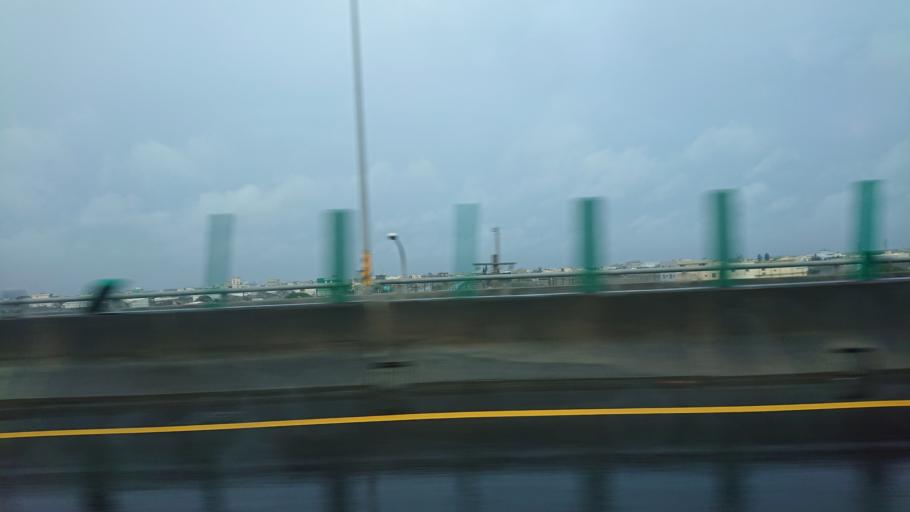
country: TW
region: Taiwan
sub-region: Changhua
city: Chang-hua
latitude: 24.1407
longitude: 120.4452
